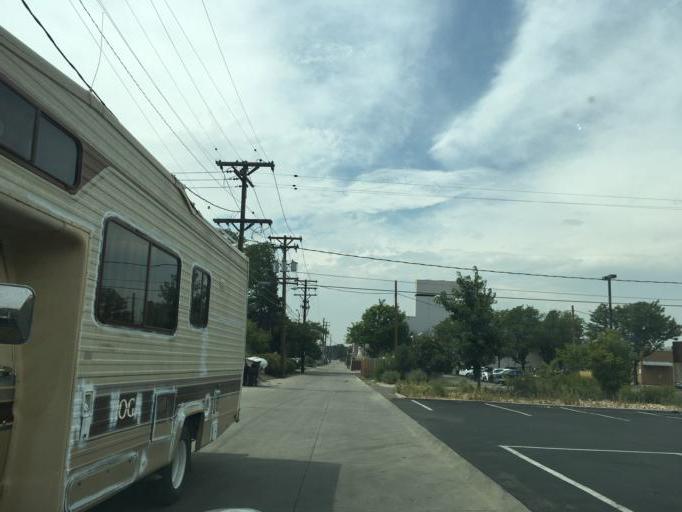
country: US
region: Colorado
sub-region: Adams County
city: Aurora
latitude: 39.7394
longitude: -104.8683
